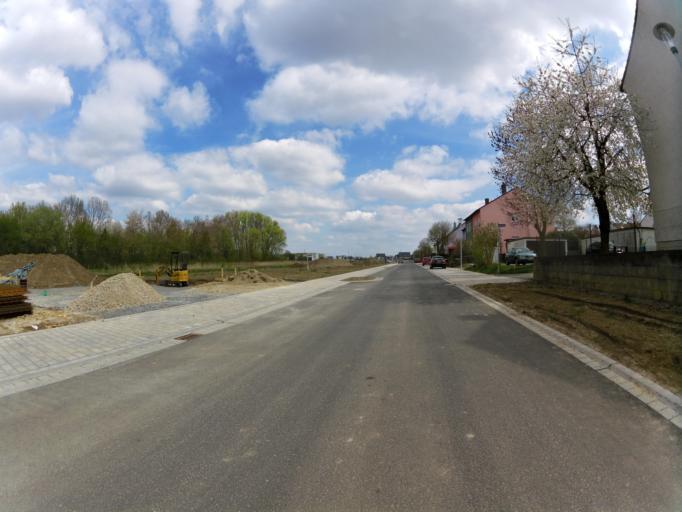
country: DE
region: Bavaria
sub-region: Regierungsbezirk Unterfranken
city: Giebelstadt
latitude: 49.6564
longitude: 9.9384
